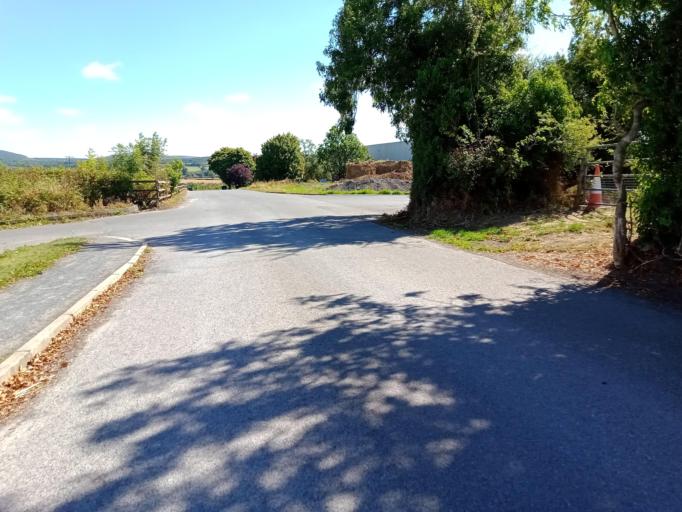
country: IE
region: Leinster
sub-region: Kilkenny
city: Thomastown
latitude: 52.5392
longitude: -7.1393
